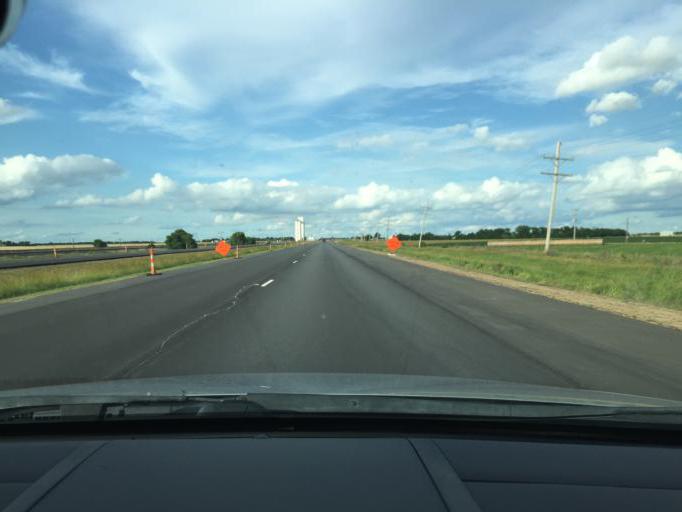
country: US
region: Kansas
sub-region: Reno County
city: South Hutchinson
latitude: 38.0010
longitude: -98.0252
